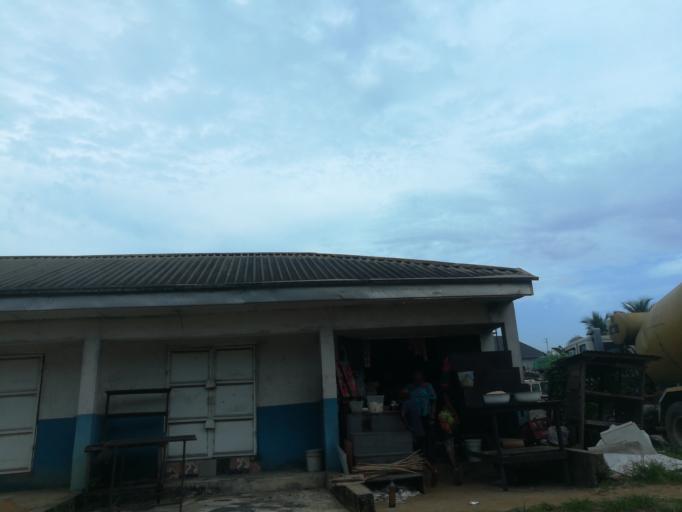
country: NG
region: Rivers
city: Port Harcourt
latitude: 4.7929
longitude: 6.9579
